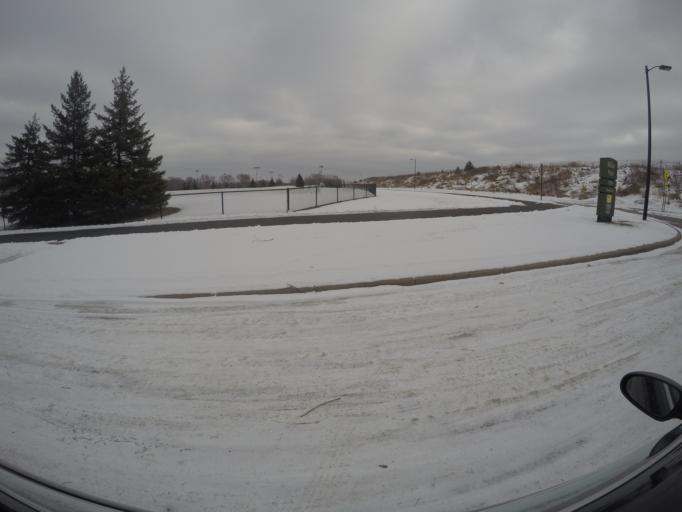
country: US
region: Minnesota
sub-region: Hennepin County
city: Eden Prairie
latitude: 44.8506
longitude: -93.4999
